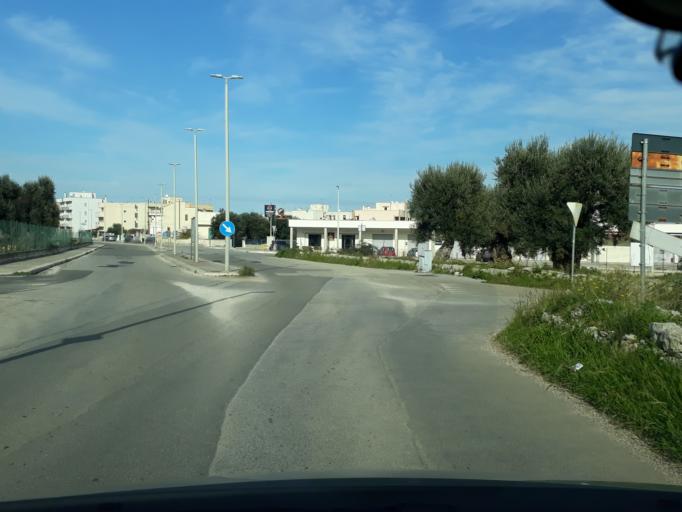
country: IT
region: Apulia
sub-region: Provincia di Brindisi
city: Fasano
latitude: 40.8269
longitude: 17.3605
